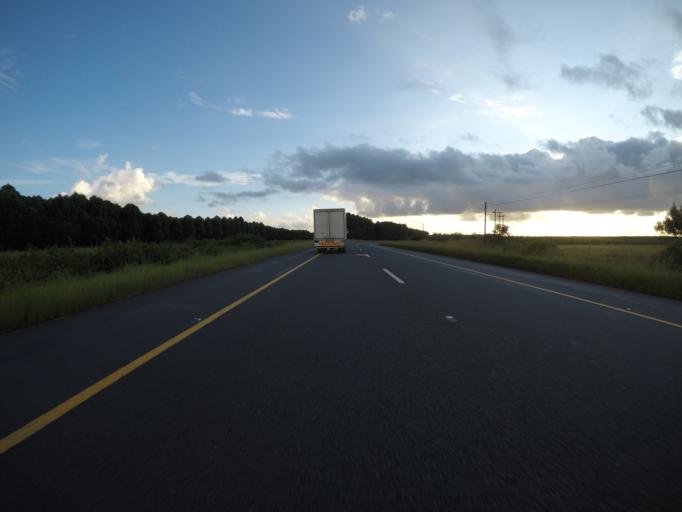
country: ZA
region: KwaZulu-Natal
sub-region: uThungulu District Municipality
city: KwaMbonambi
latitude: -28.5756
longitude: 32.1062
